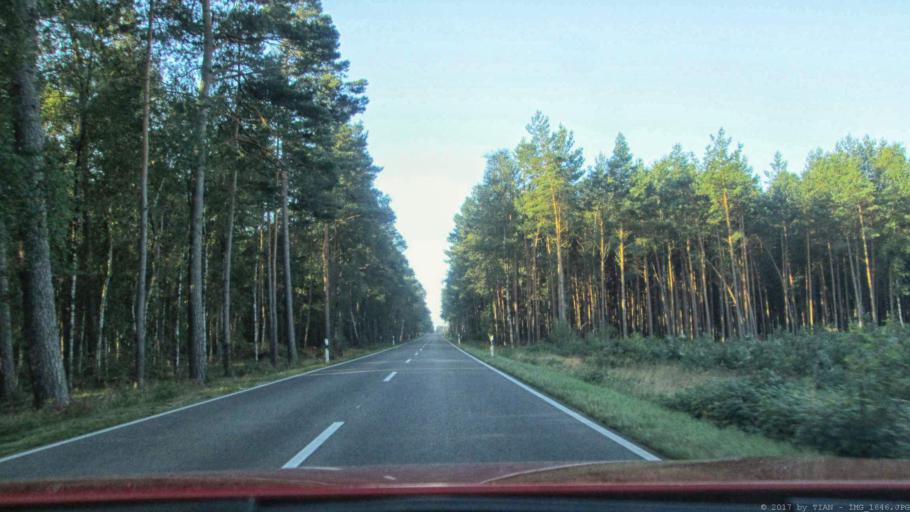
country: DE
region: Lower Saxony
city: Bergfeld
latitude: 52.6039
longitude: 10.8032
